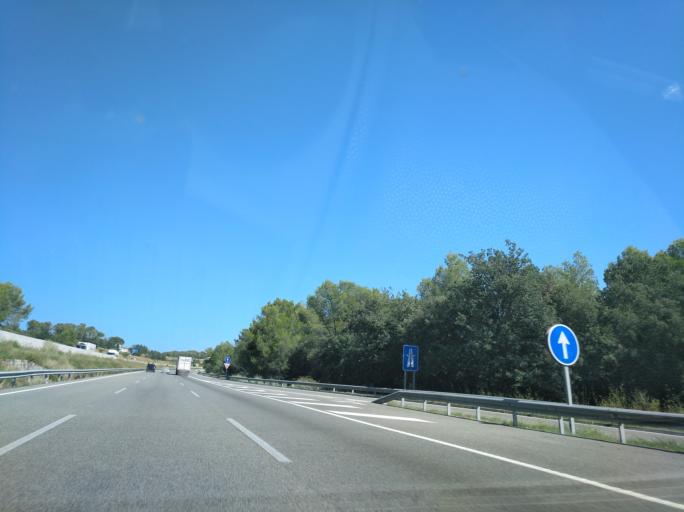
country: ES
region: Catalonia
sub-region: Provincia de Girona
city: Cervia de Ter
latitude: 42.0813
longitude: 2.8900
